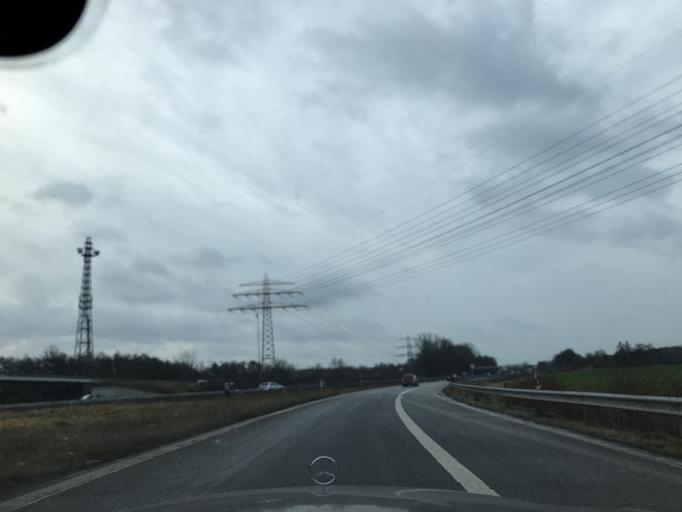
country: DE
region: Schleswig-Holstein
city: Barsbuettel
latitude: 53.5596
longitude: 10.1558
